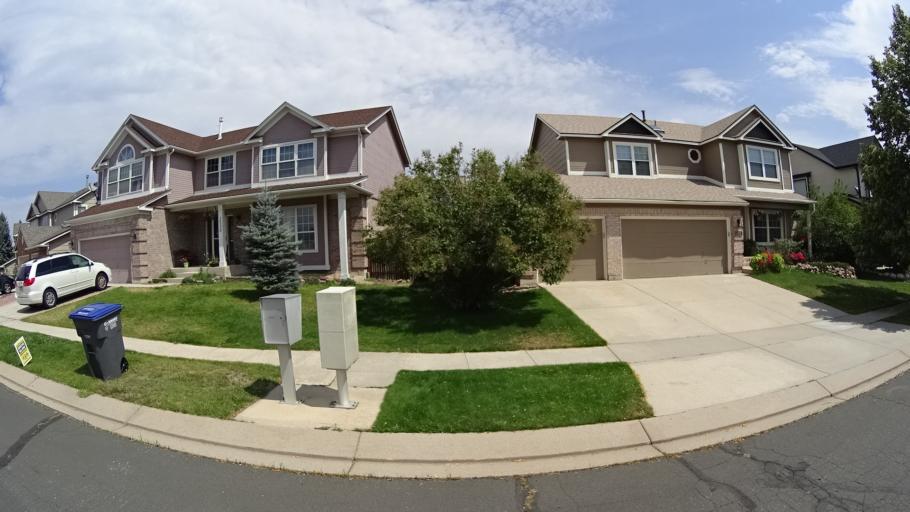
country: US
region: Colorado
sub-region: El Paso County
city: Air Force Academy
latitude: 38.9618
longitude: -104.7784
